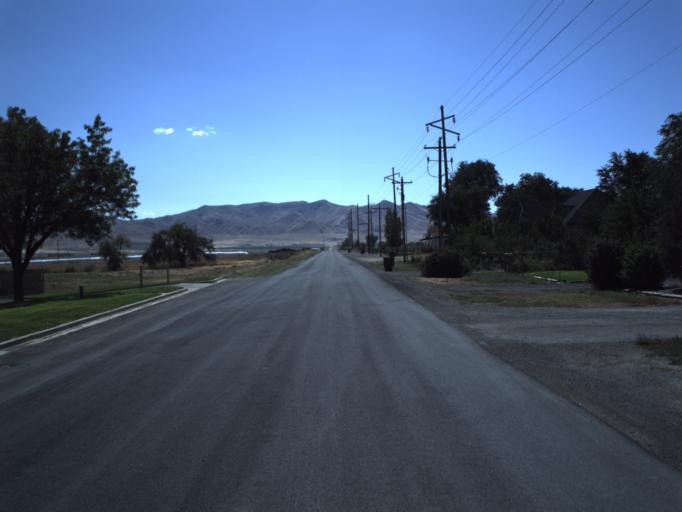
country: US
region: Utah
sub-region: Utah County
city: Genola
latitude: 39.9498
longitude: -111.9561
